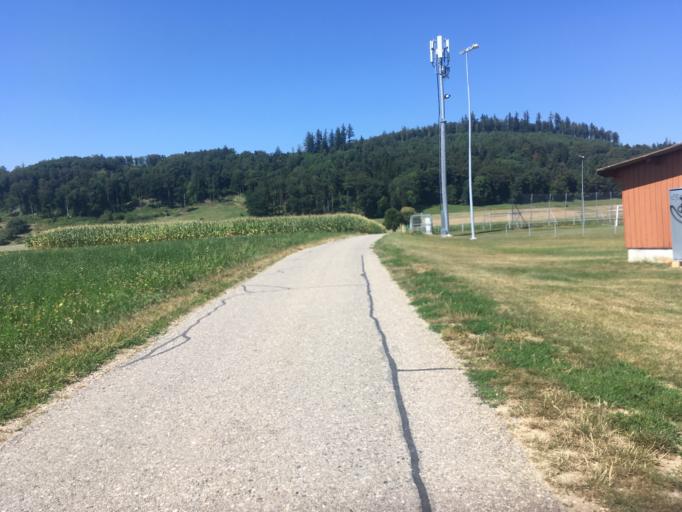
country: CH
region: Bern
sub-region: Biel/Bienne District
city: Meinisberg
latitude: 47.1155
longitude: 7.3571
